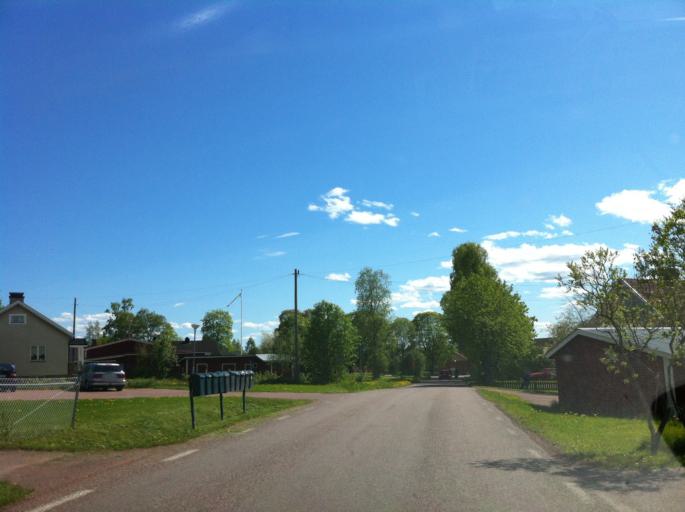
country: SE
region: Dalarna
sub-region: Mora Kommun
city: Mora
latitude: 61.0007
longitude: 14.6263
